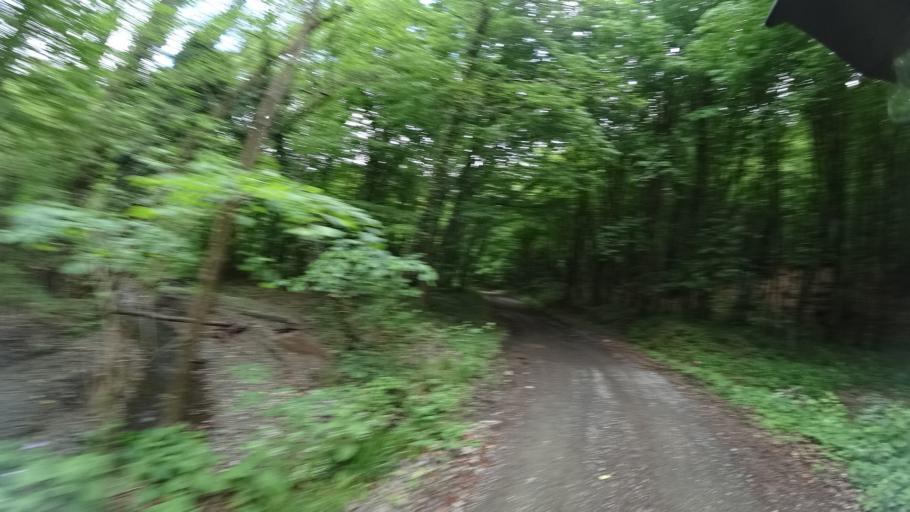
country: HR
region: Krapinsko-Zagorska
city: Oroslavje
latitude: 45.9356
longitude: 15.9334
